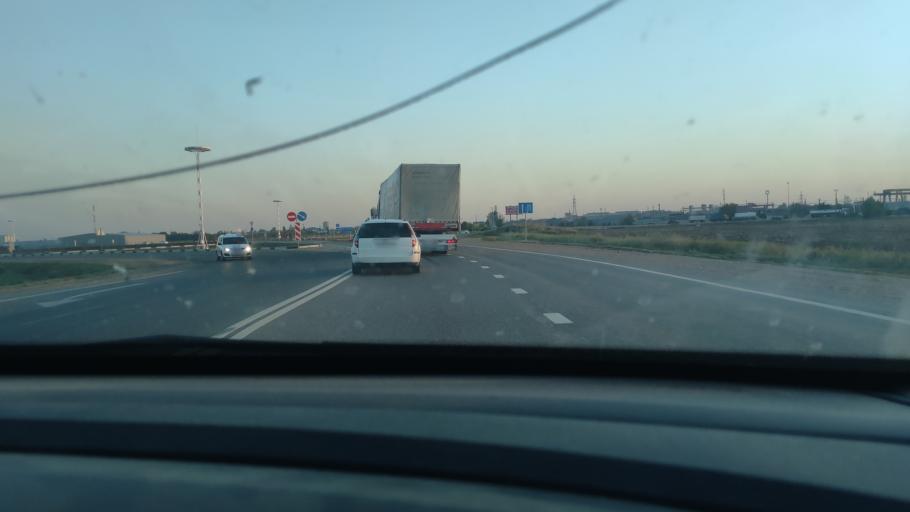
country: RU
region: Krasnodarskiy
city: Timashevsk
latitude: 45.6411
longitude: 38.9699
